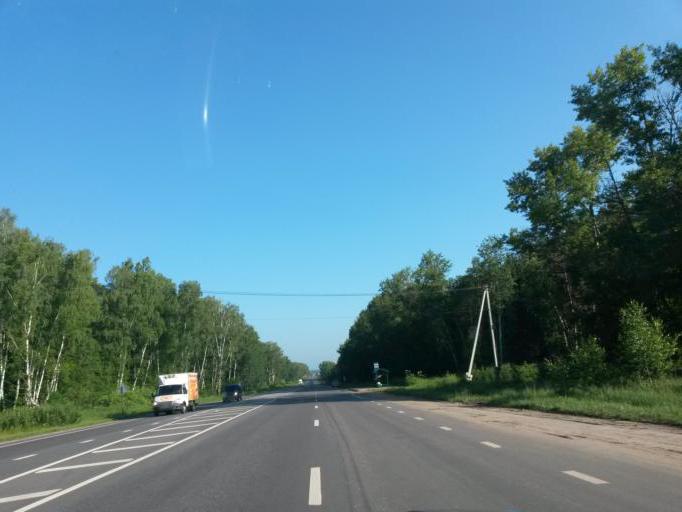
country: RU
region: Moskovskaya
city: Barybino
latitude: 55.2340
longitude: 37.8639
